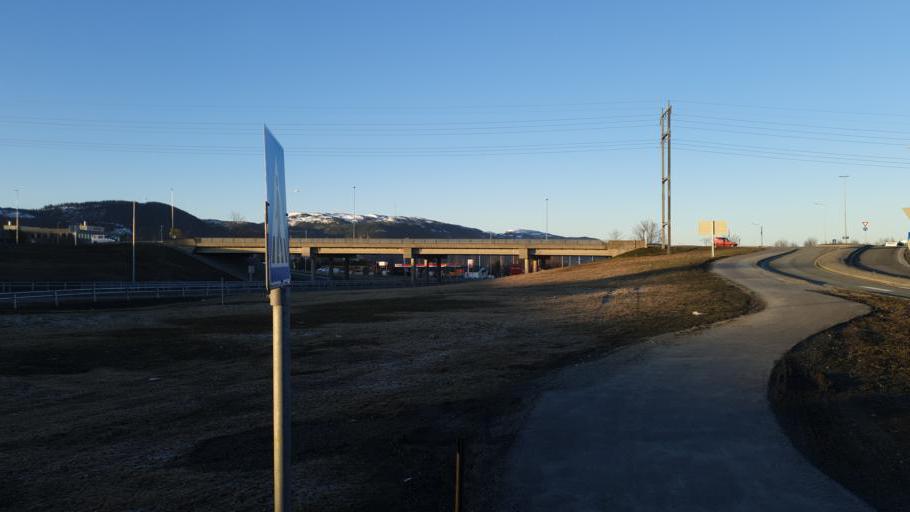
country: NO
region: Sor-Trondelag
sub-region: Melhus
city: Melhus
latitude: 63.3347
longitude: 10.3565
